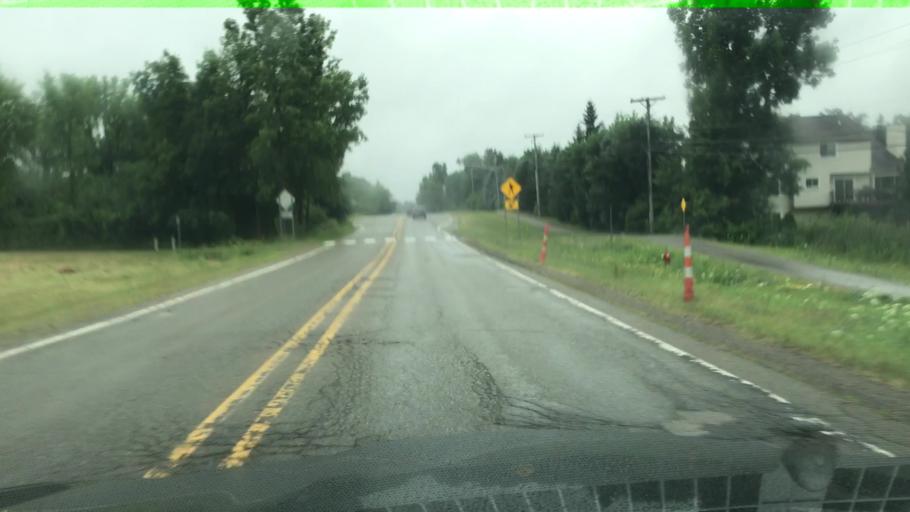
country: US
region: Michigan
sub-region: Oakland County
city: Lake Orion
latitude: 42.7334
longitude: -83.2881
